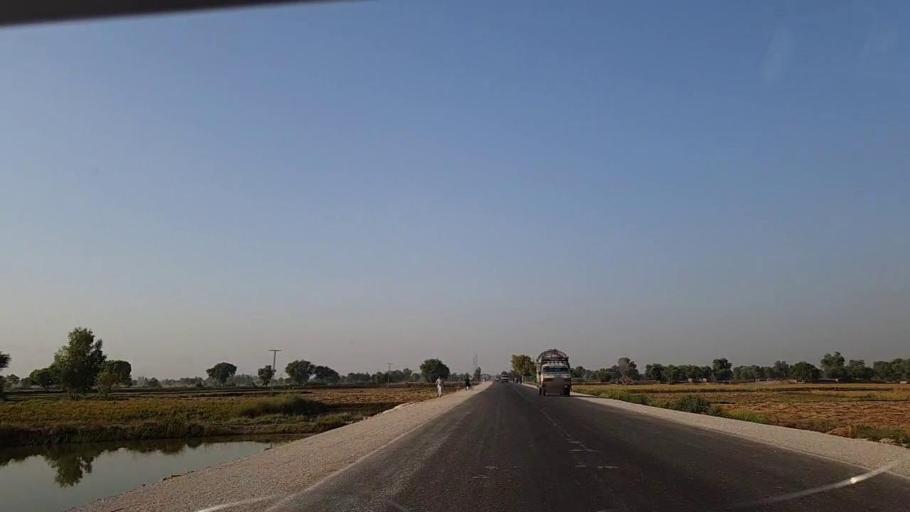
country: PK
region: Sindh
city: Rustam jo Goth
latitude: 27.9531
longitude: 68.8085
